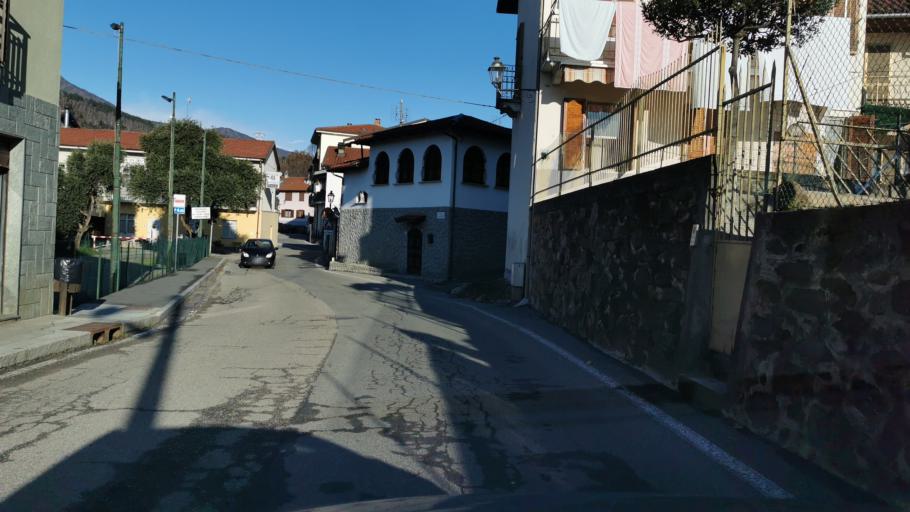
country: IT
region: Piedmont
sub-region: Provincia di Torino
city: La Cassa
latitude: 45.1800
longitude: 7.5169
